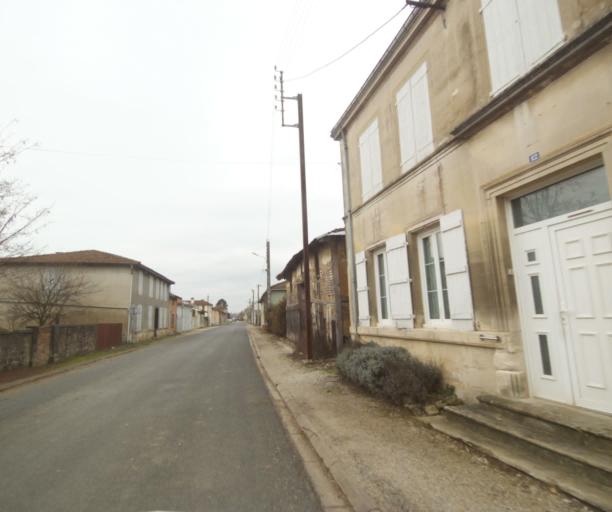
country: FR
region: Champagne-Ardenne
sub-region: Departement de la Haute-Marne
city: Villiers-en-Lieu
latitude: 48.6429
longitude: 4.8714
